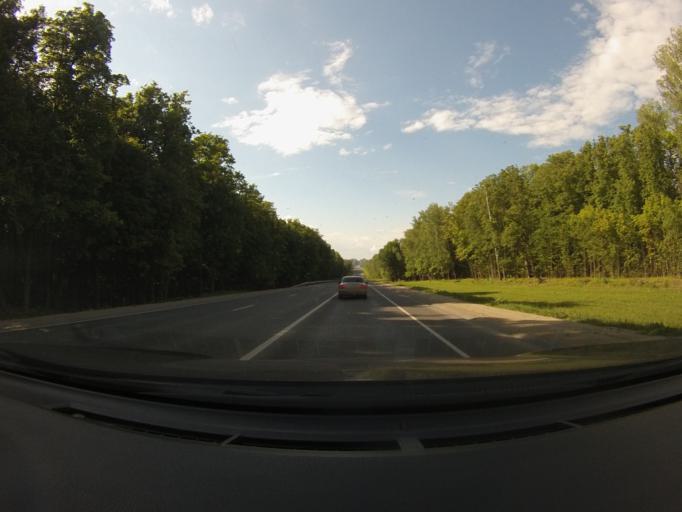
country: RU
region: Tula
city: Gorelki
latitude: 54.2853
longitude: 37.5857
